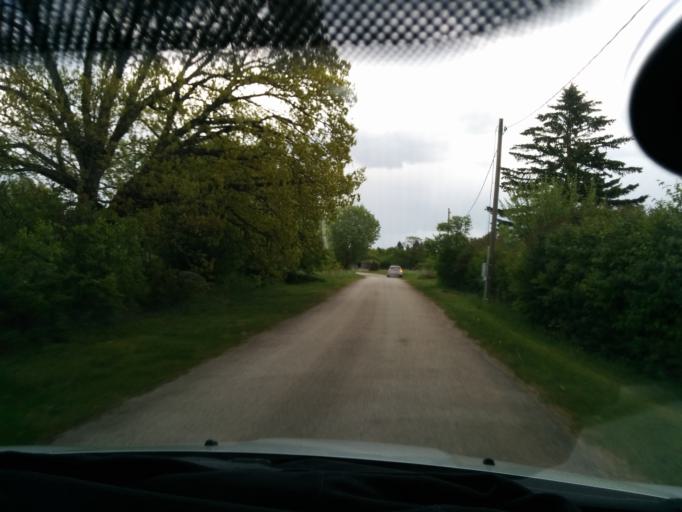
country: EE
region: Harju
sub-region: Loksa linn
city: Loksa
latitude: 59.6546
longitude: 25.6871
